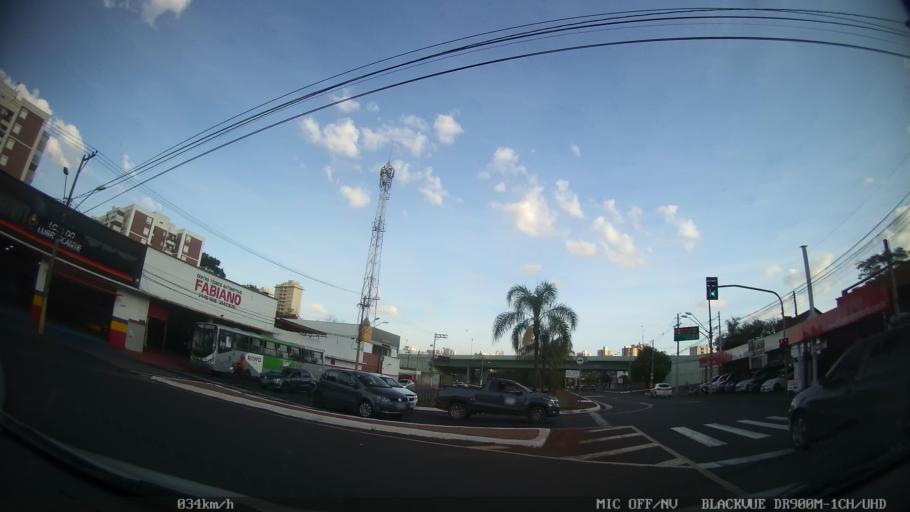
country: BR
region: Sao Paulo
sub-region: Ribeirao Preto
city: Ribeirao Preto
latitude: -21.1933
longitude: -47.7980
